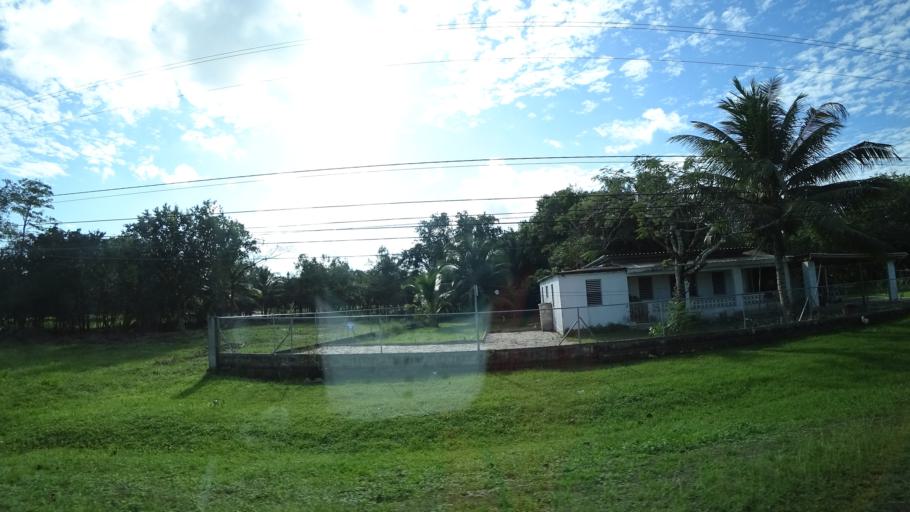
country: BZ
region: Belize
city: Belize City
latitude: 17.5614
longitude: -88.4051
